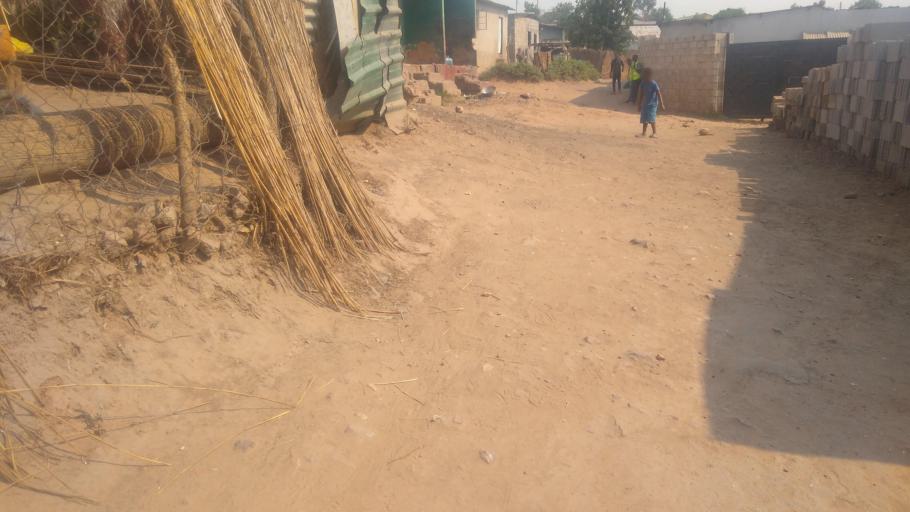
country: ZM
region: Lusaka
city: Lusaka
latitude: -15.4429
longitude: 28.3881
